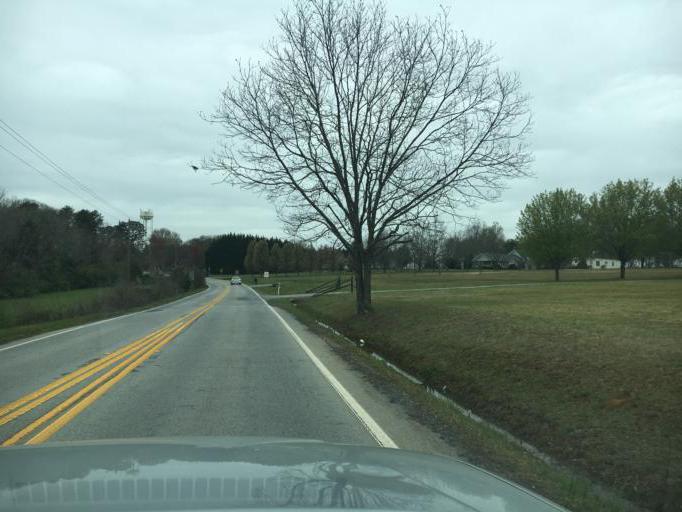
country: US
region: South Carolina
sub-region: Spartanburg County
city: Duncan
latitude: 34.9816
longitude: -82.1644
